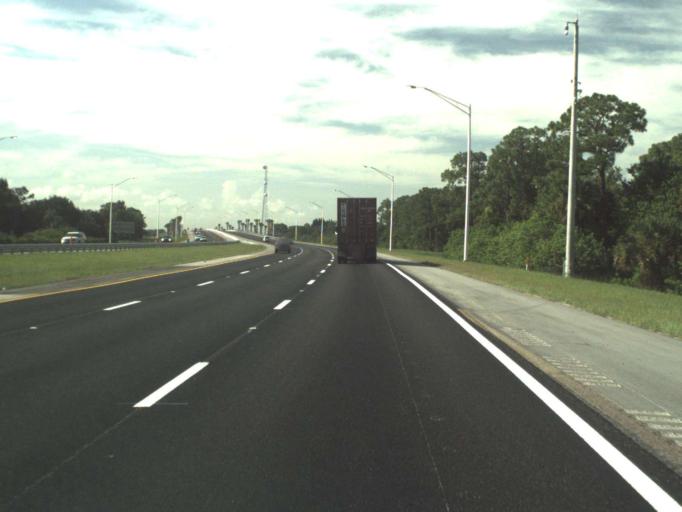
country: US
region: Florida
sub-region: Indian River County
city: West Vero Corridor
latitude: 27.6176
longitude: -80.5154
